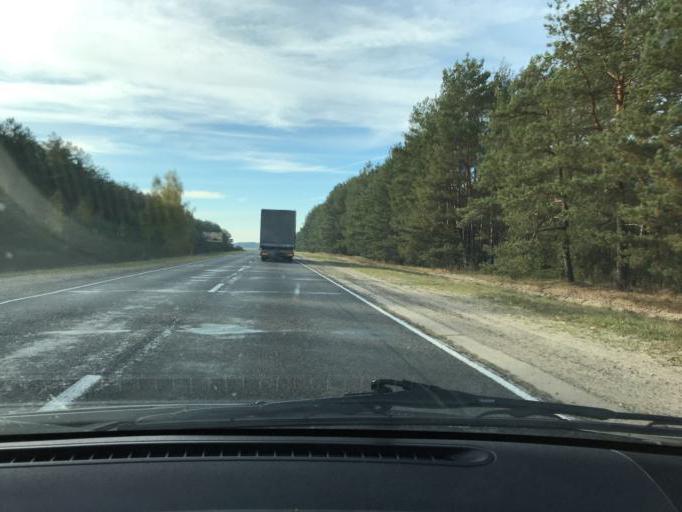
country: BY
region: Brest
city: Horad Pinsk
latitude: 52.1521
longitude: 25.8354
